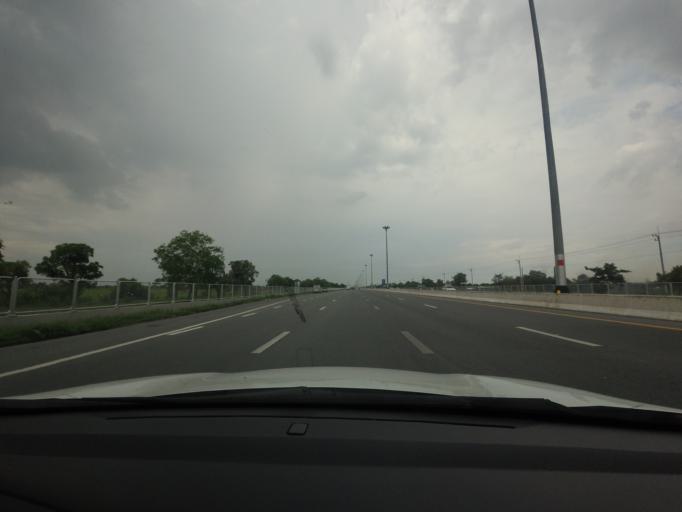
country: TH
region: Pathum Thani
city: Khlong Luang
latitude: 14.1310
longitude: 100.6697
